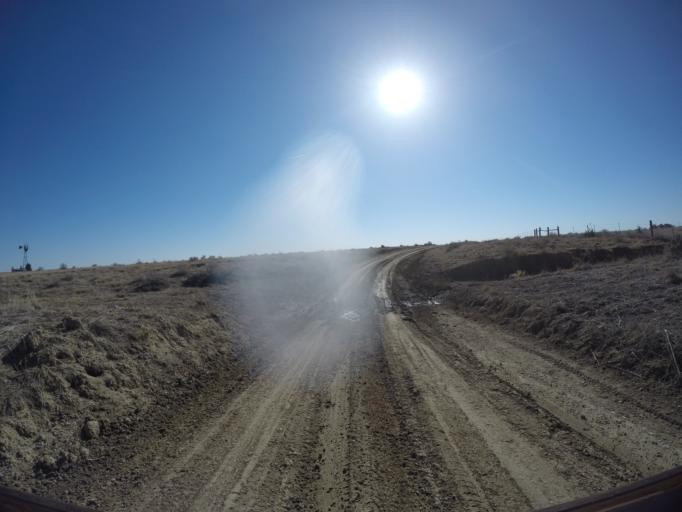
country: US
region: Colorado
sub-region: Otero County
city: La Junta
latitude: 37.6878
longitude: -103.6204
